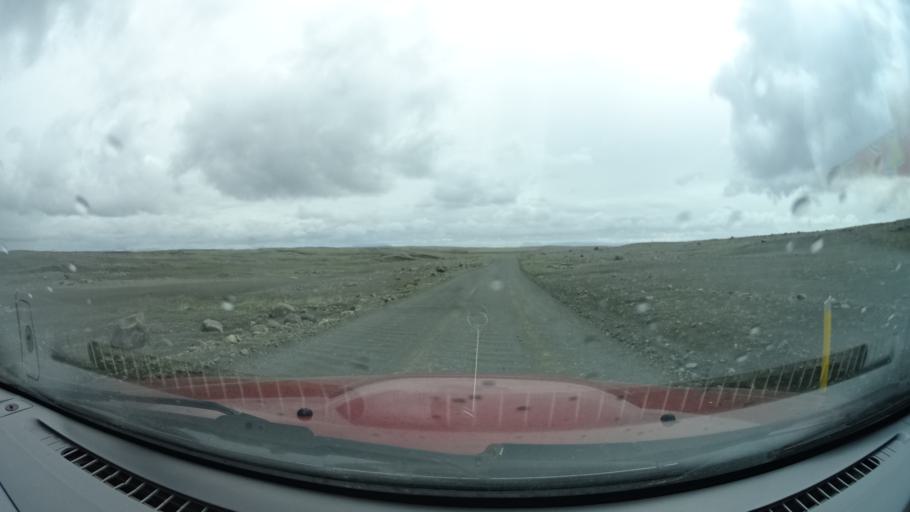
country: IS
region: Northeast
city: Laugar
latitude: 65.7570
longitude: -16.3314
